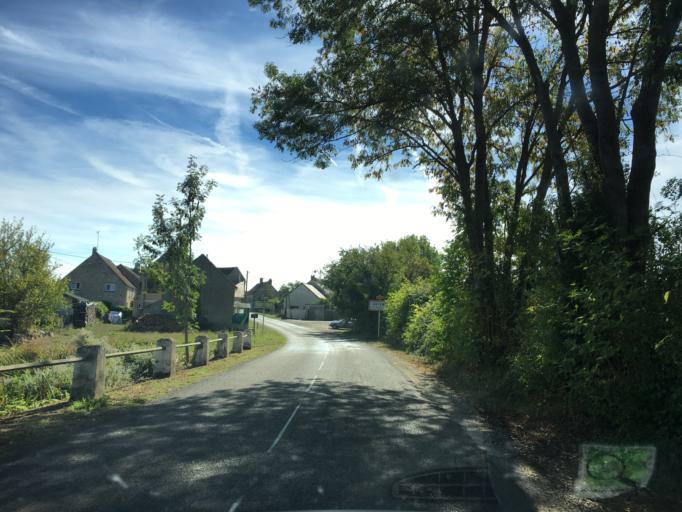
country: FR
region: Bourgogne
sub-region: Departement de l'Yonne
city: Vermenton
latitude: 47.5873
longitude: 3.7064
